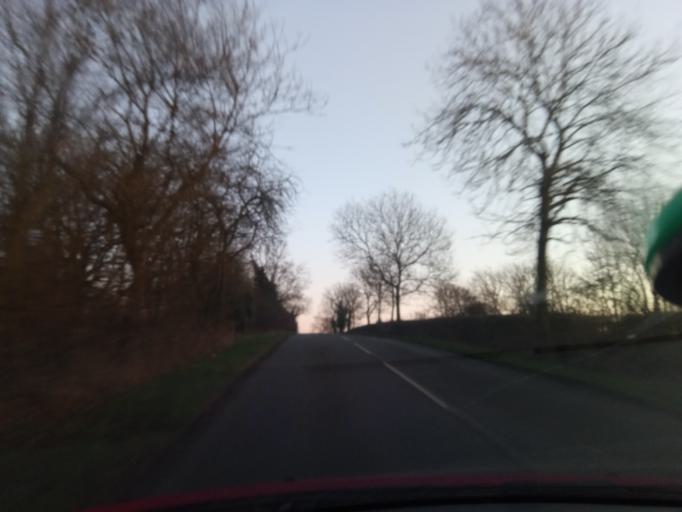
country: GB
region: England
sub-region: Leicestershire
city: Sileby
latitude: 52.7556
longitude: -1.0962
